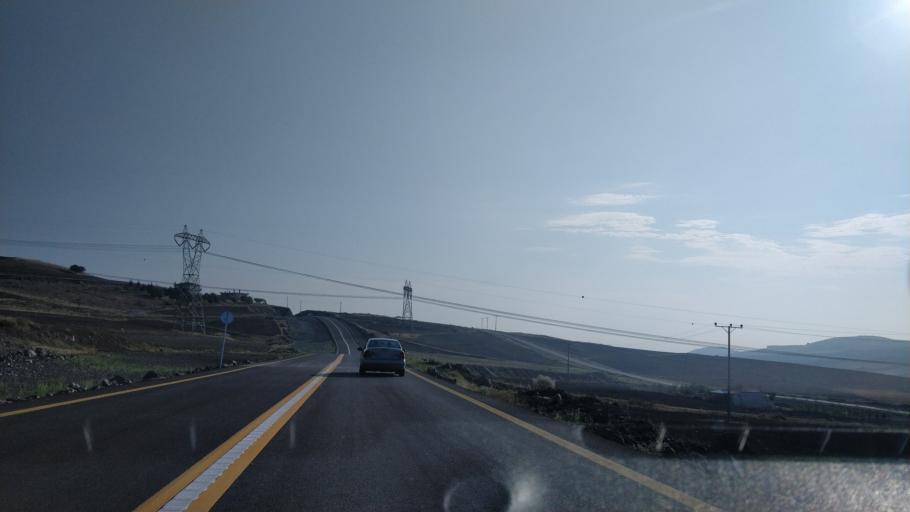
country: TR
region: Ankara
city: Etimesgut
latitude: 39.8646
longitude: 32.5858
